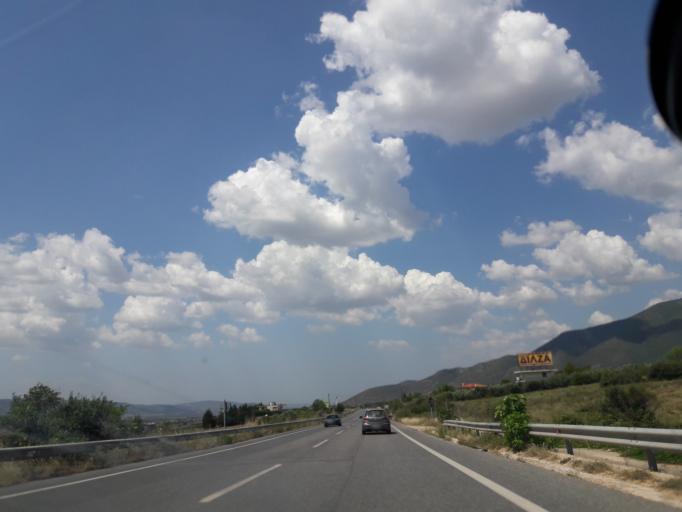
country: GR
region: Central Macedonia
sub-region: Nomos Chalkidikis
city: Galatista
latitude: 40.4648
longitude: 23.2630
